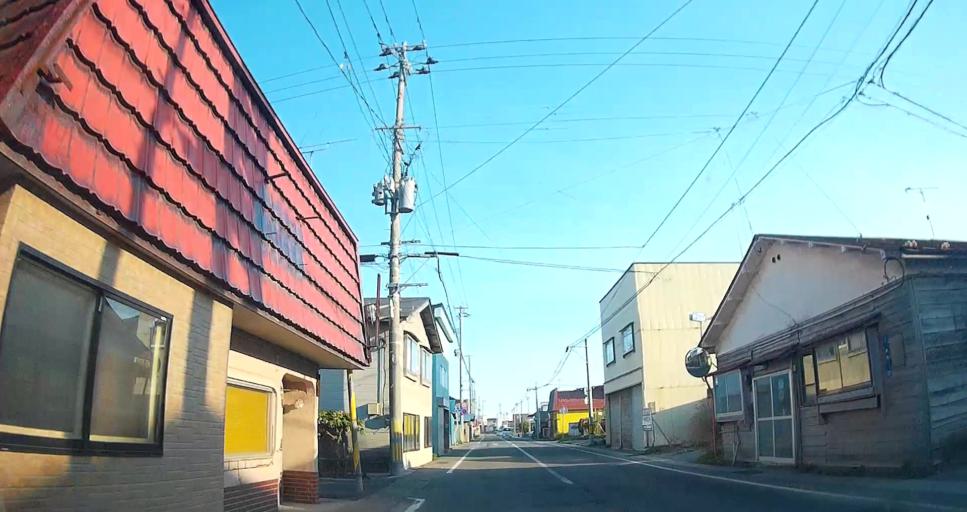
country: JP
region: Aomori
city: Mutsu
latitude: 41.2888
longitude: 141.2113
